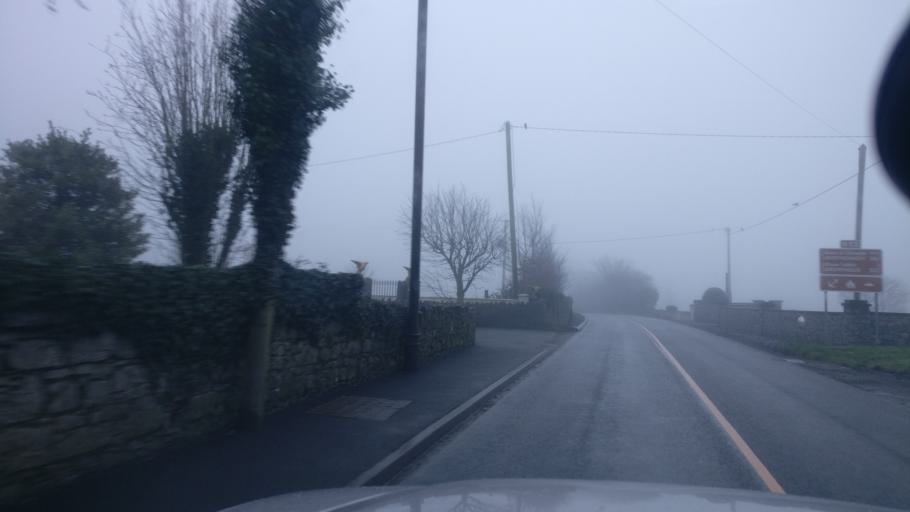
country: IE
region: Munster
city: Nenagh Bridge
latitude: 52.9876
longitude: -8.1324
